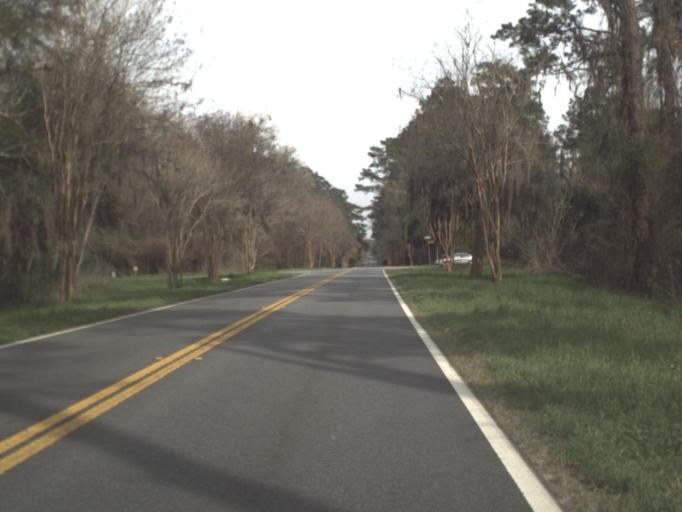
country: US
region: Florida
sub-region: Jefferson County
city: Monticello
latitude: 30.5288
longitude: -83.9919
